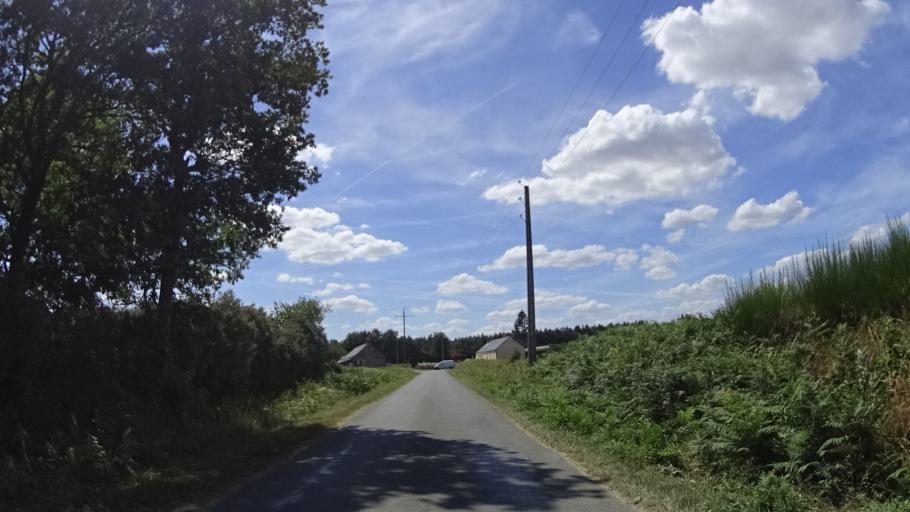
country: FR
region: Pays de la Loire
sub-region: Departement de Maine-et-Loire
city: Cande
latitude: 47.6152
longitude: -1.0349
